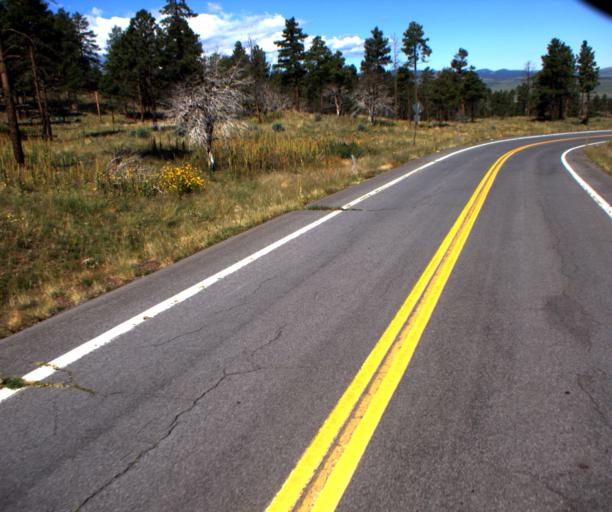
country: US
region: Arizona
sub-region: Apache County
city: Eagar
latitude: 34.0689
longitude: -109.3507
